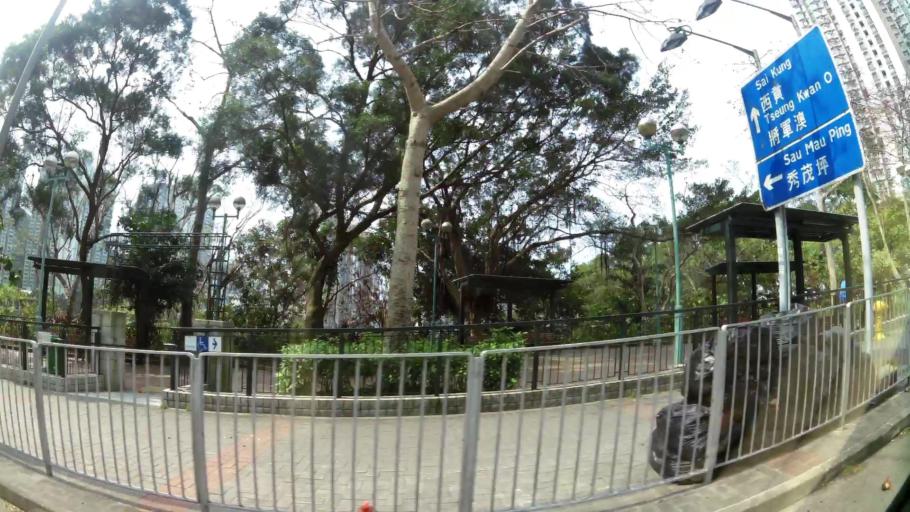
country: HK
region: Kowloon City
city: Kowloon
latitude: 22.3155
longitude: 114.2370
